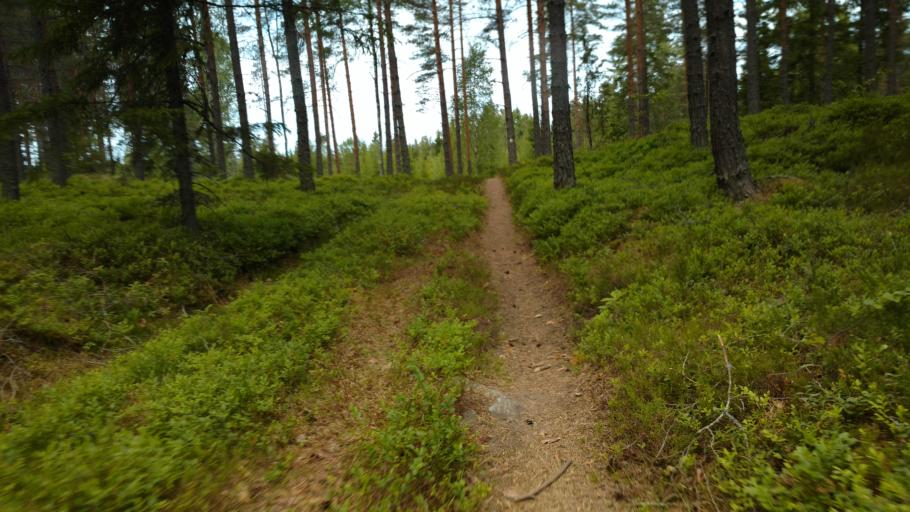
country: FI
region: Uusimaa
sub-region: Raaseporin
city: Pohja
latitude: 60.1162
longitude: 23.5688
